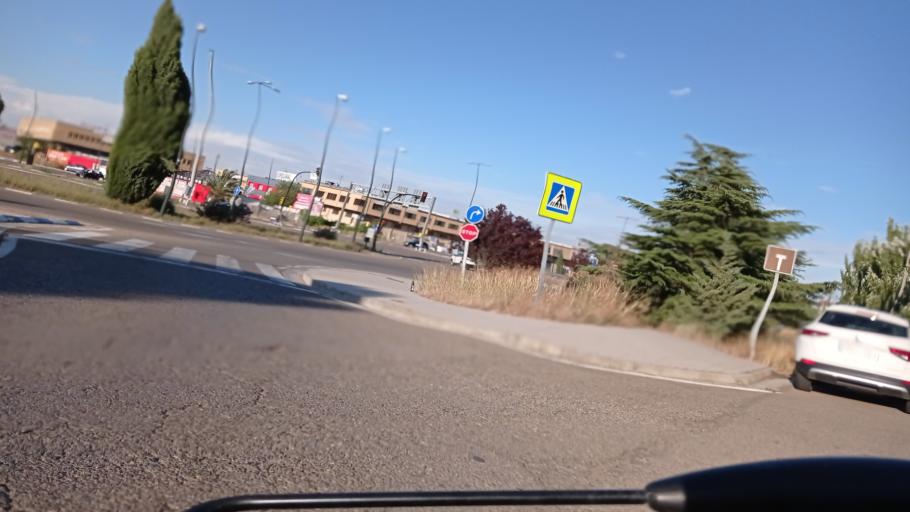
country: ES
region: Aragon
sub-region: Provincia de Zaragoza
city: Oliver-Valdefierro, Oliver, Valdefierro
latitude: 41.6726
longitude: -0.9516
